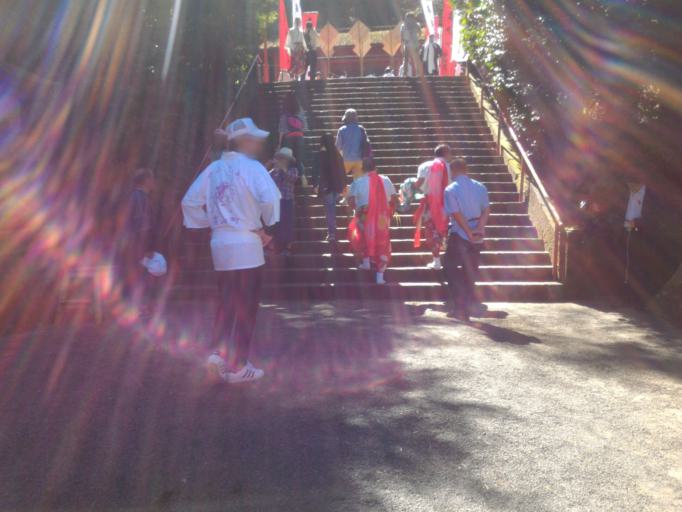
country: JP
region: Kagoshima
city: Kanoya
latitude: 31.3437
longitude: 130.9469
